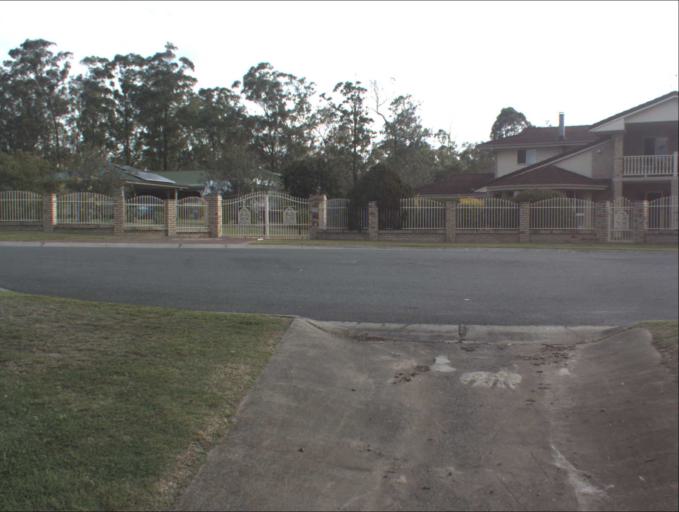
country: AU
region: Queensland
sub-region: Brisbane
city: Forest Lake
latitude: -27.6621
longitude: 152.9926
